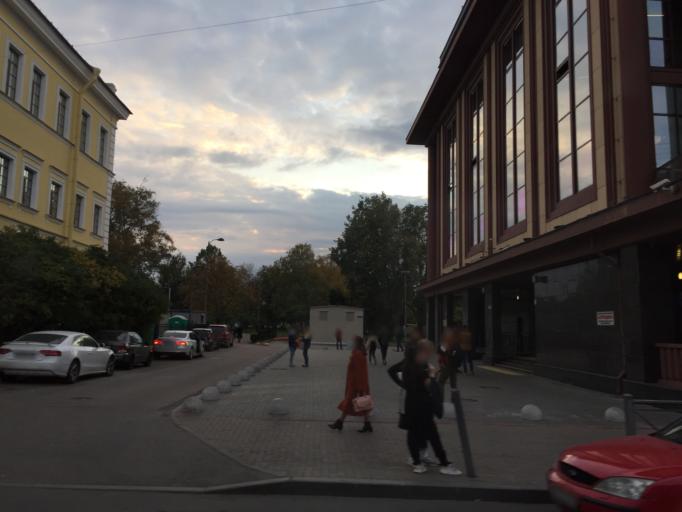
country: RU
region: St.-Petersburg
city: Centralniy
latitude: 59.9222
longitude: 30.3362
